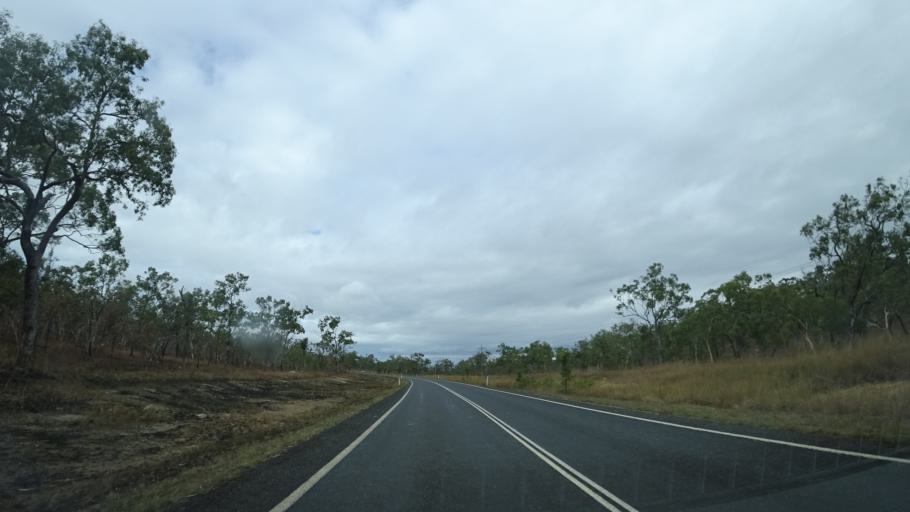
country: AU
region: Queensland
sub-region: Tablelands
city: Mareeba
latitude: -16.7768
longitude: 145.3404
